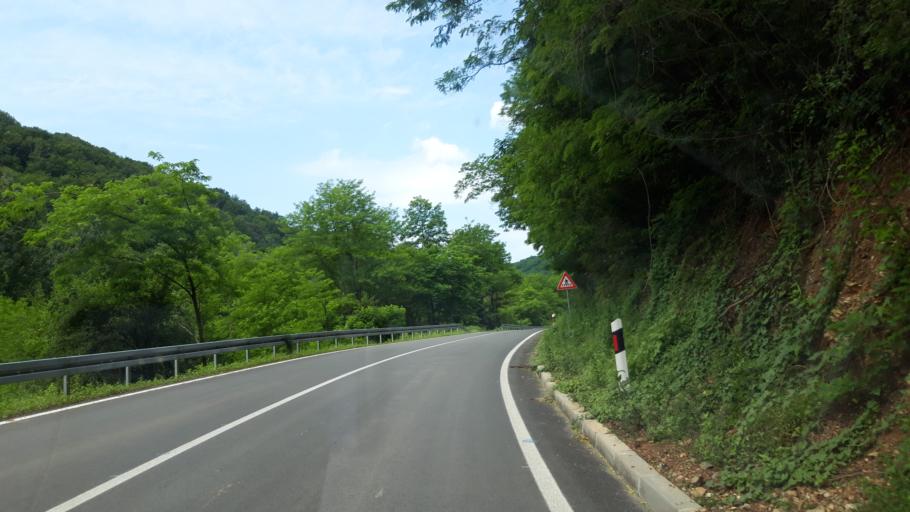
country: RS
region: Central Serbia
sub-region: Jablanicki Okrug
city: Vlasotince
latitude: 42.9765
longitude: 22.2521
